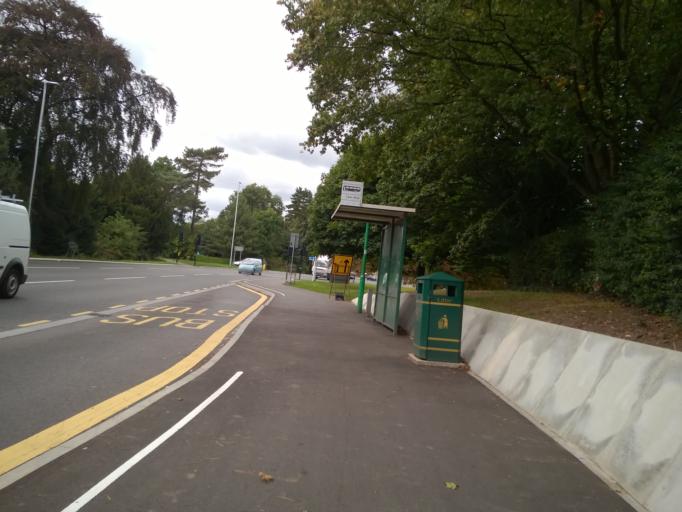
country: GB
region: England
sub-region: Leicestershire
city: Glenfield
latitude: 52.6570
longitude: -1.1933
